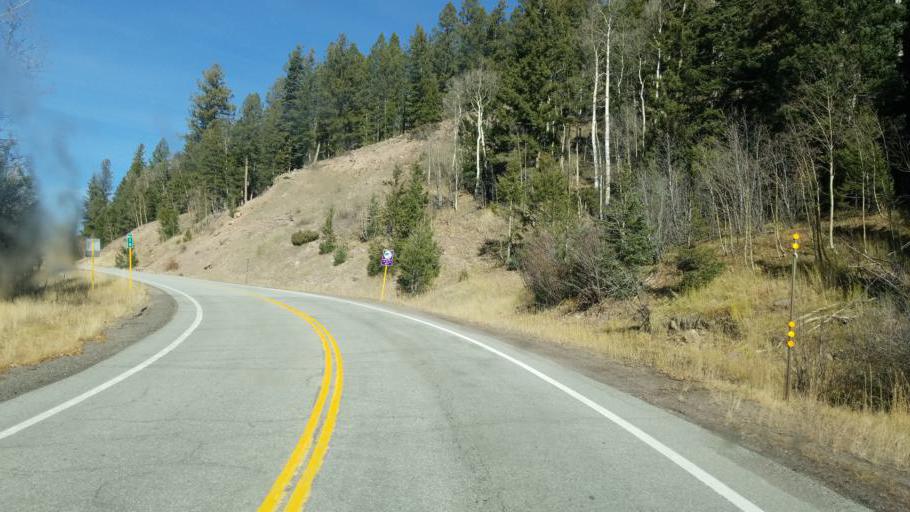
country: US
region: New Mexico
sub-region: Rio Arriba County
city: Chama
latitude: 37.1102
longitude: -106.3742
